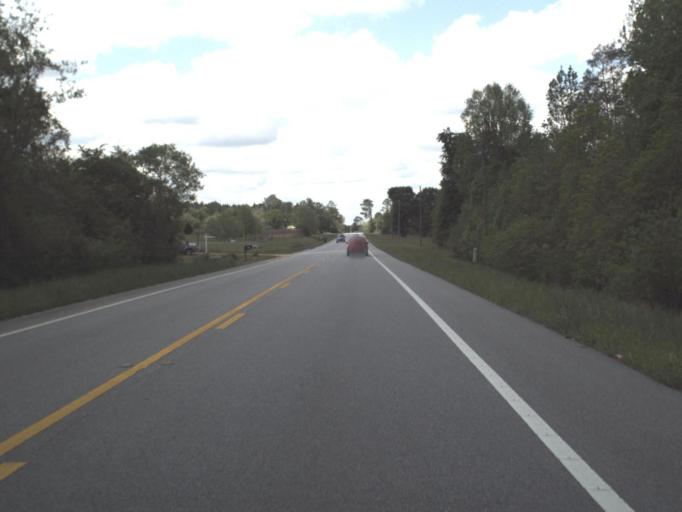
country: US
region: Florida
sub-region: Escambia County
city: Molino
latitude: 30.7809
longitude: -87.4022
